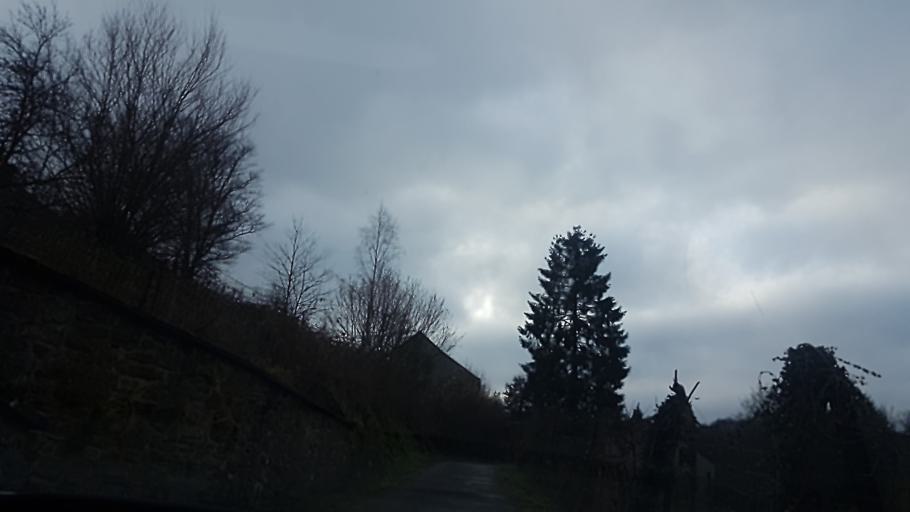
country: BE
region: Wallonia
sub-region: Province de Namur
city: Couvin
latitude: 50.0688
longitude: 4.6067
